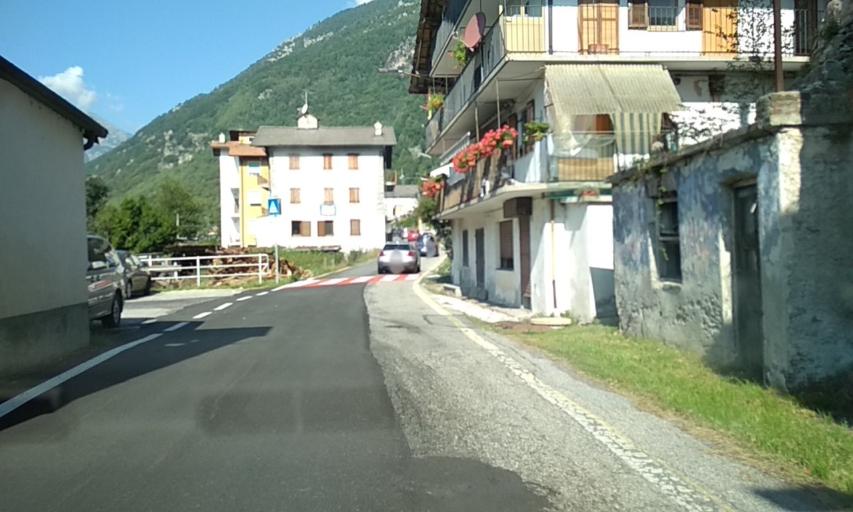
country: IT
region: Piedmont
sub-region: Provincia di Torino
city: Locana
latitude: 45.4330
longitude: 7.4286
